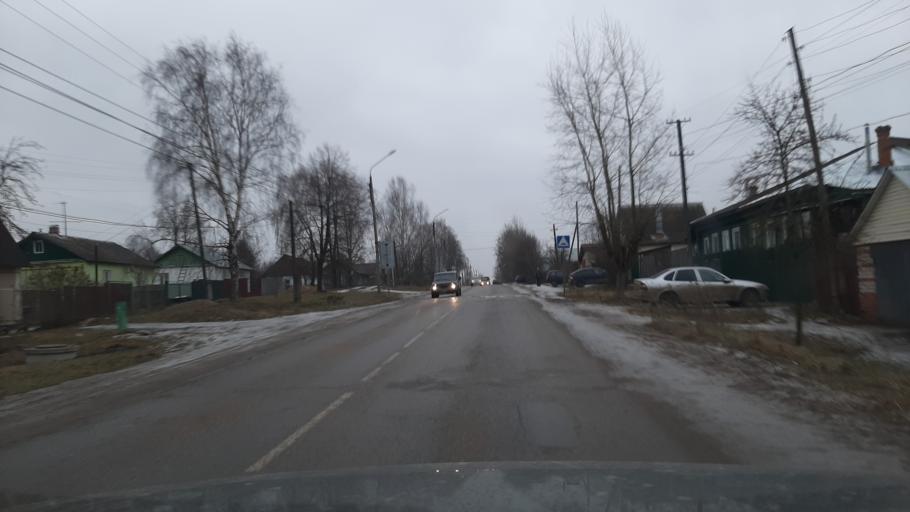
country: RU
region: Ivanovo
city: Shuya
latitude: 56.8735
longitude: 41.3524
